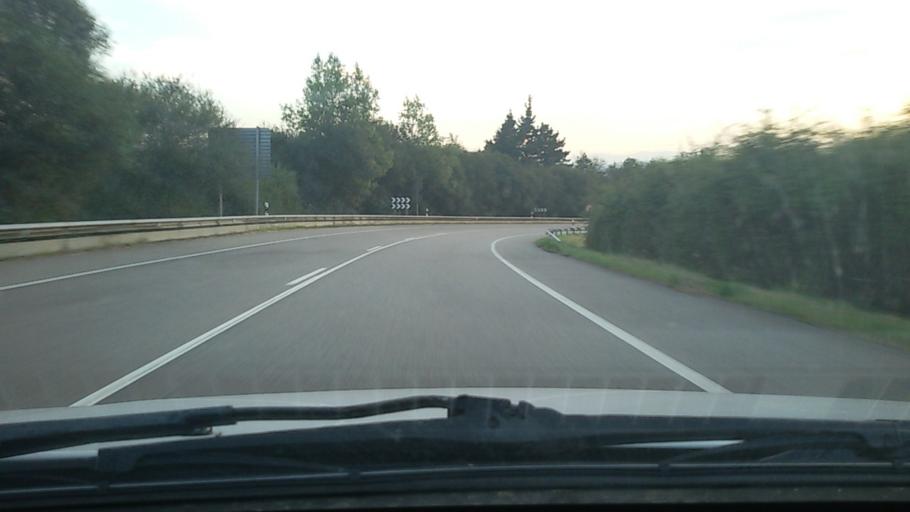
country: ES
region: Asturias
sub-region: Province of Asturias
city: Norena
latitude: 43.3827
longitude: -5.7281
